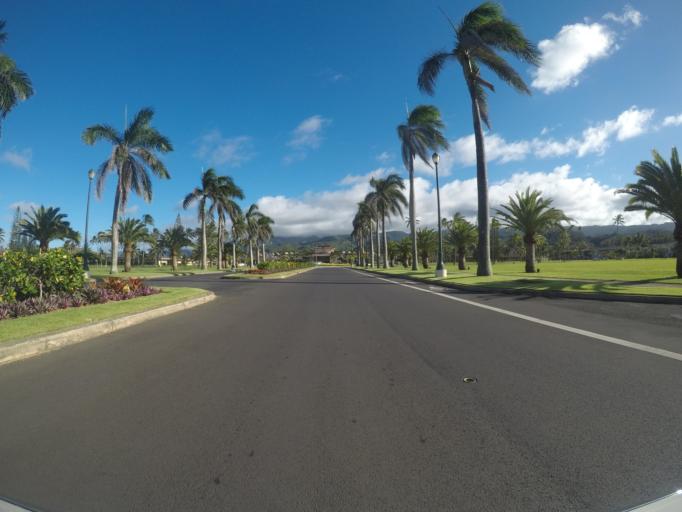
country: US
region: Hawaii
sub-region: Honolulu County
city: La'ie
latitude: 21.6438
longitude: -157.9251
